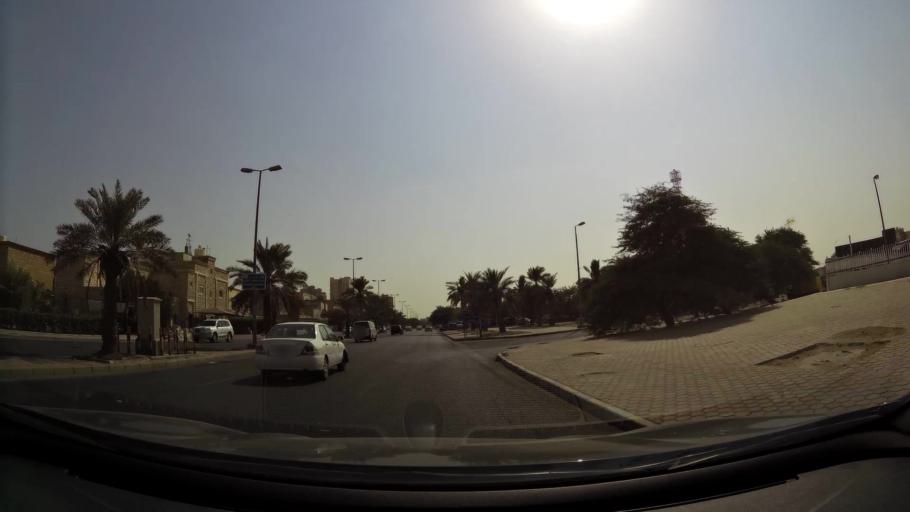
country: KW
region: Al Ahmadi
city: Al Fahahil
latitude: 29.0877
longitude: 48.1225
